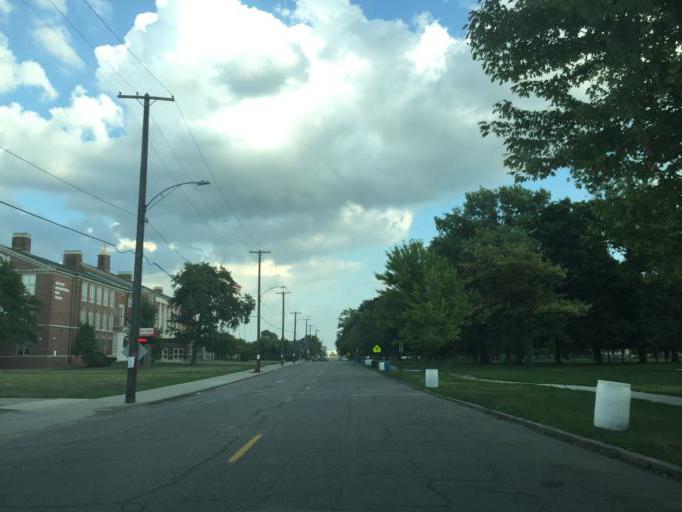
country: US
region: Michigan
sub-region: Wayne County
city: Detroit
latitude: 42.3198
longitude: -83.0932
